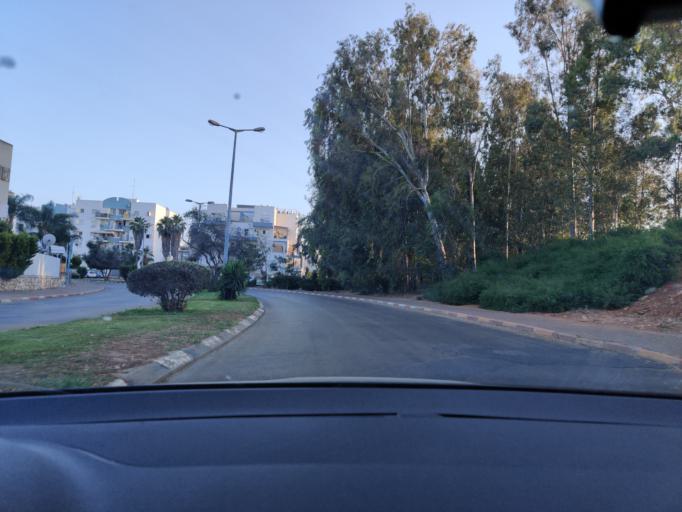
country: IL
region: Haifa
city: Hadera
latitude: 32.4752
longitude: 34.9518
